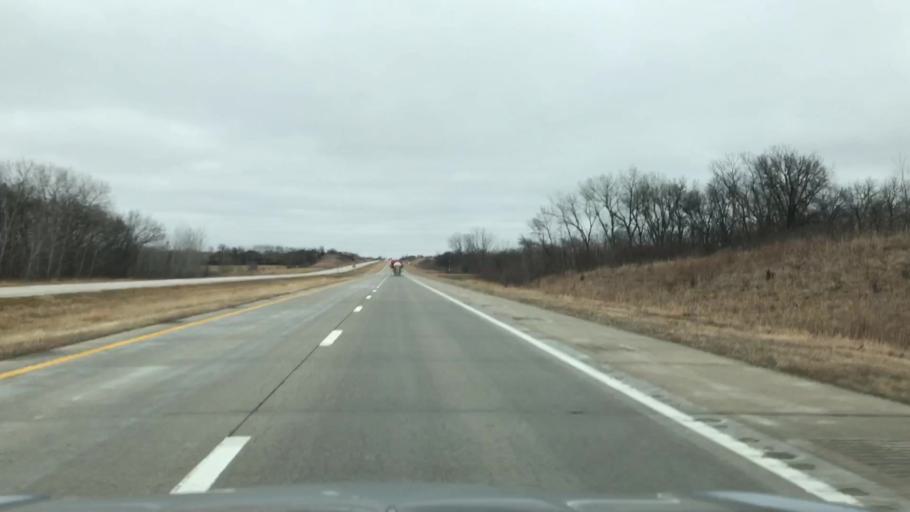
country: US
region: Missouri
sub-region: Caldwell County
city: Hamilton
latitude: 39.7343
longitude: -93.9670
